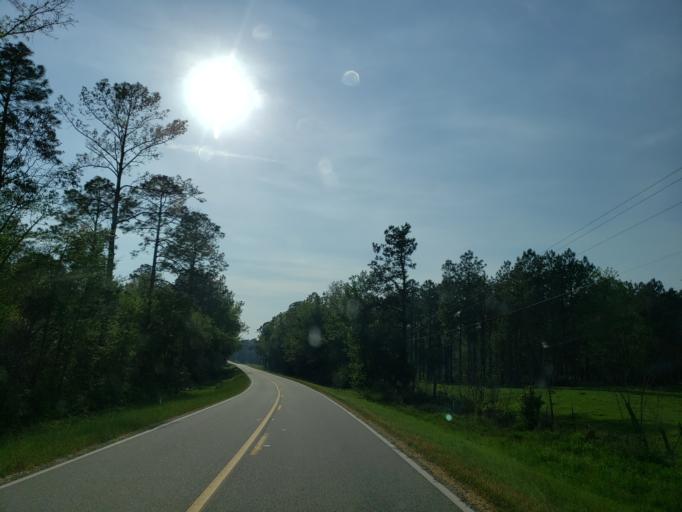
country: US
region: Georgia
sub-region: Tift County
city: Tifton
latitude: 31.5586
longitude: -83.5021
